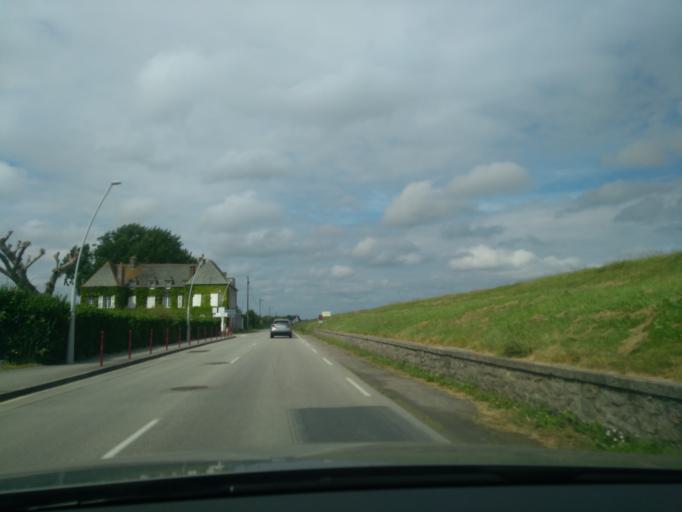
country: FR
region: Lower Normandy
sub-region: Departement de la Manche
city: Saint-Vaast-la-Hougue
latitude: 49.5931
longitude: -1.2667
